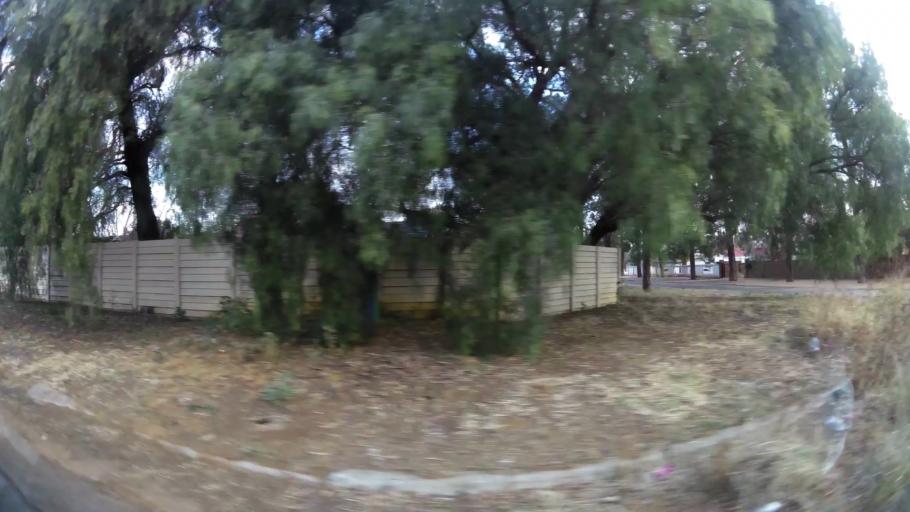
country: ZA
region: Orange Free State
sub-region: Lejweleputswa District Municipality
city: Welkom
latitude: -27.9781
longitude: 26.7216
